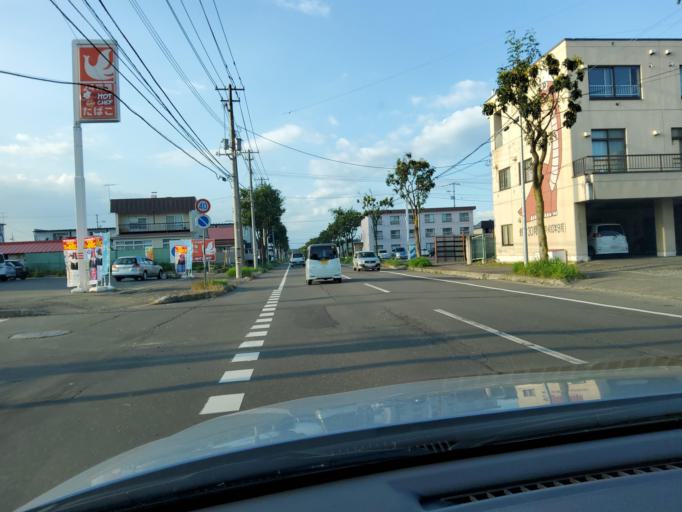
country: JP
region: Hokkaido
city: Obihiro
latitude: 42.9331
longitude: 143.1847
